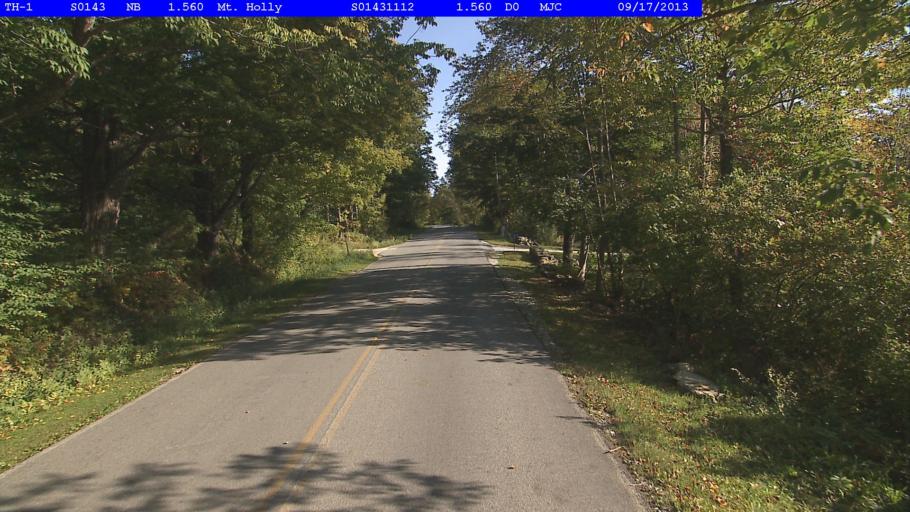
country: US
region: Vermont
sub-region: Rutland County
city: Rutland
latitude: 43.4215
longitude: -72.8203
